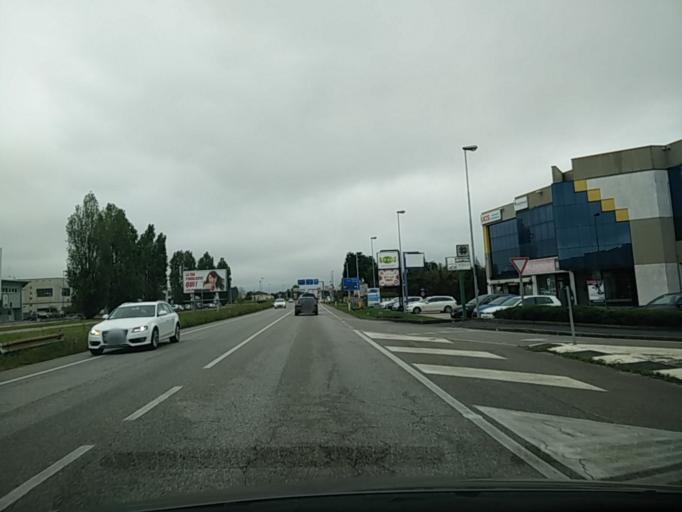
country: IT
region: Veneto
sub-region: Provincia di Treviso
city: Vedelago
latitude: 45.6850
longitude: 11.9965
